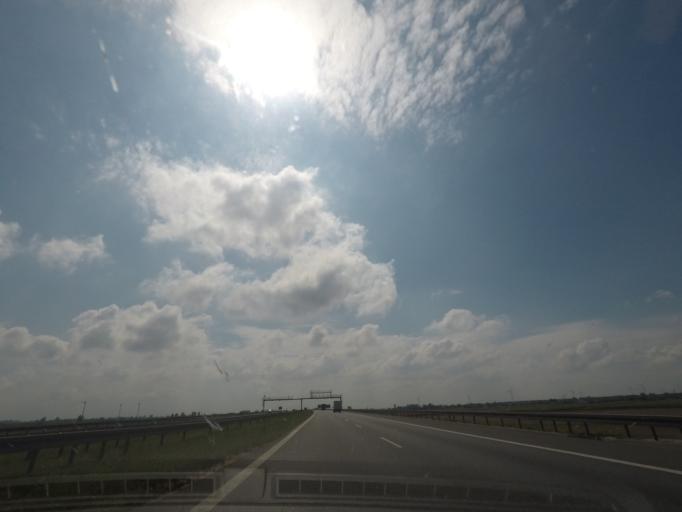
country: PL
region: Lodz Voivodeship
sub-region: Powiat kutnowski
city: Krzyzanow
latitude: 52.2340
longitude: 19.4550
